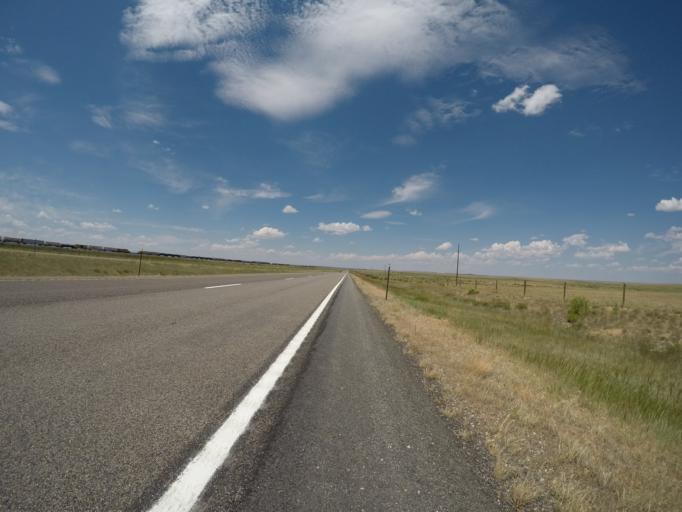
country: US
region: Wyoming
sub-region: Albany County
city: Laramie
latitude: 41.6156
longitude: -105.7418
